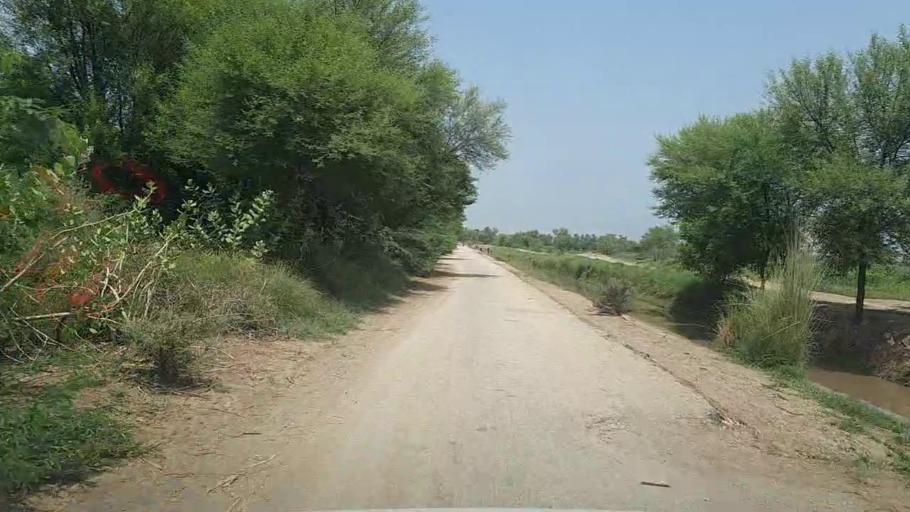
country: PK
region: Sindh
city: Karaundi
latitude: 26.8987
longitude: 68.3315
